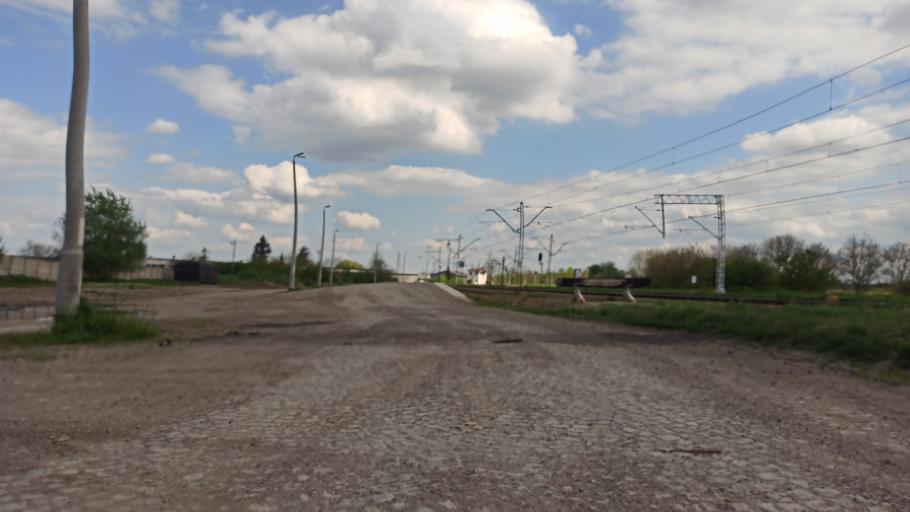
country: PL
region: Subcarpathian Voivodeship
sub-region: Powiat jaroslawski
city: Radymno
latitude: 49.9393
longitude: 22.8306
